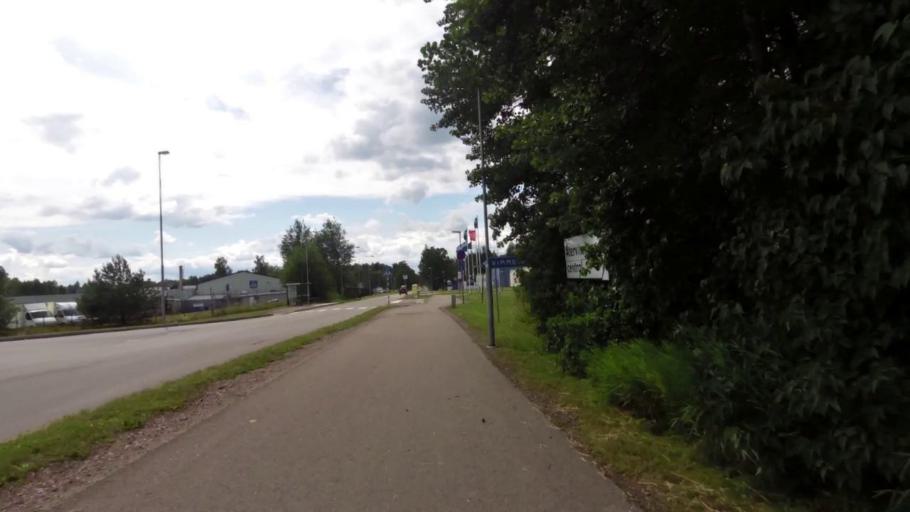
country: SE
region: OEstergoetland
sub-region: Linkopings Kommun
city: Malmslatt
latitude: 58.4008
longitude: 15.5513
